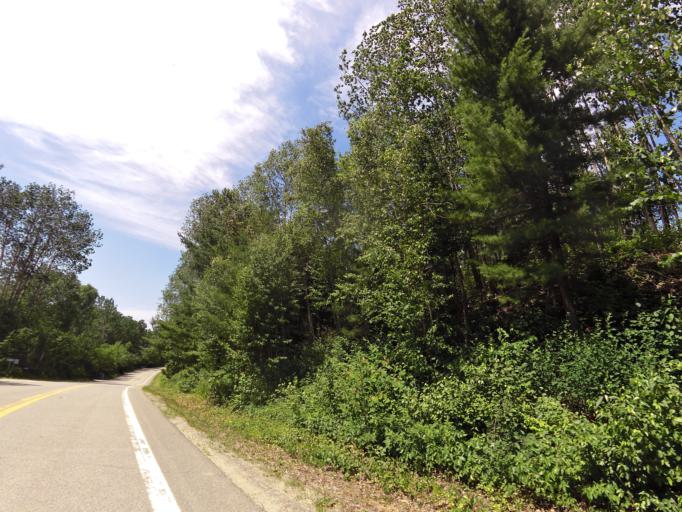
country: CA
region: Quebec
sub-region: Abitibi-Temiscamingue
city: Ville-Marie
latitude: 47.2912
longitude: -79.4481
